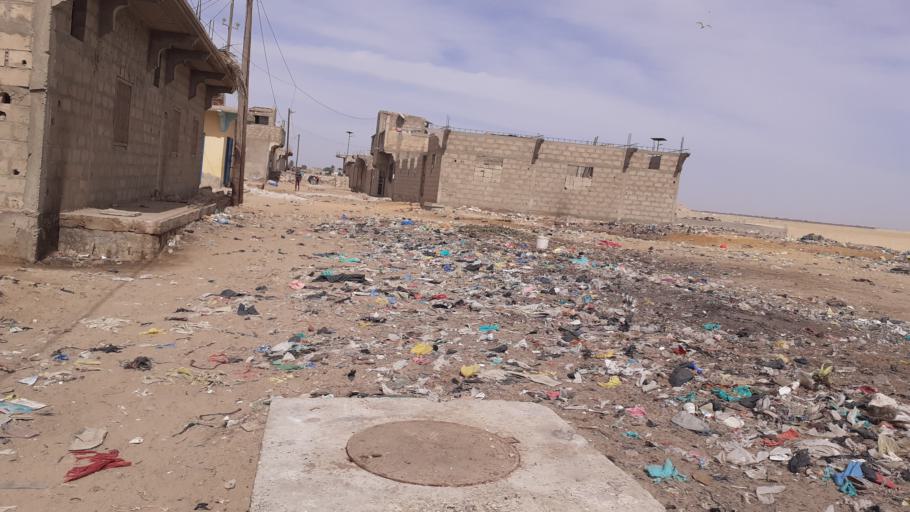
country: SN
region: Saint-Louis
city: Saint-Louis
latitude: 16.0239
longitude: -16.4831
